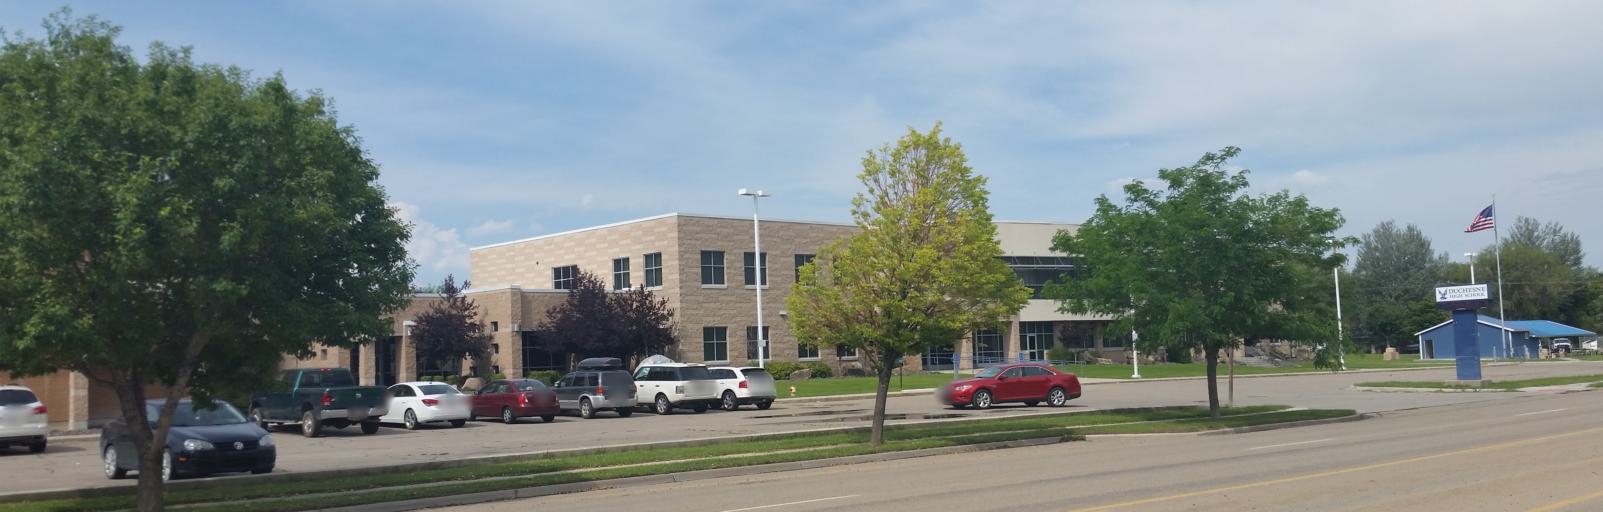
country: US
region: Utah
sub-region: Duchesne County
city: Duchesne
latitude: 40.1634
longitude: -110.4055
